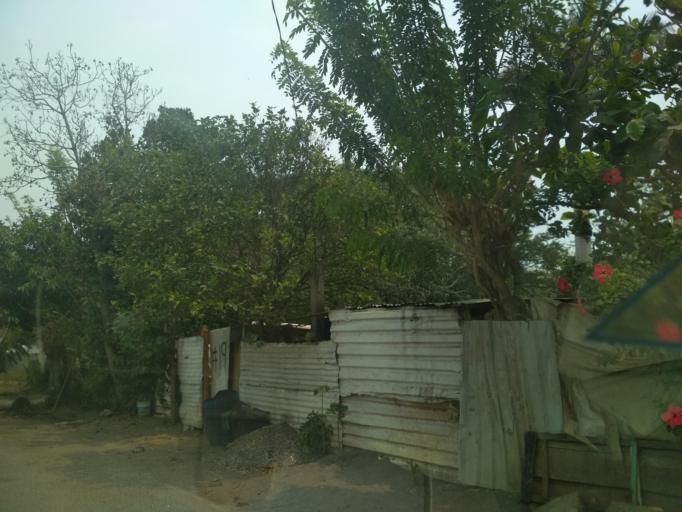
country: MX
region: Veracruz
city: Paso del Toro
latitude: 19.0506
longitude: -96.1525
